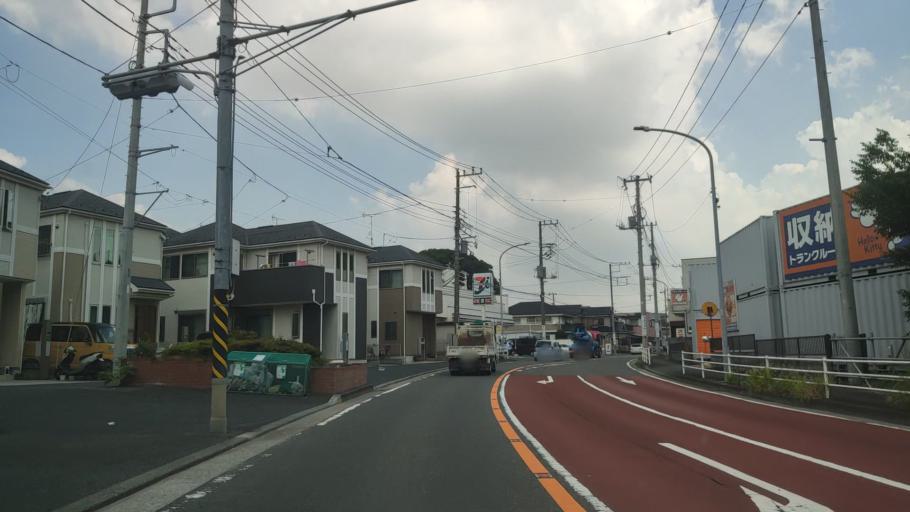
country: JP
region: Kanagawa
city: Minami-rinkan
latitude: 35.4325
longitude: 139.5126
